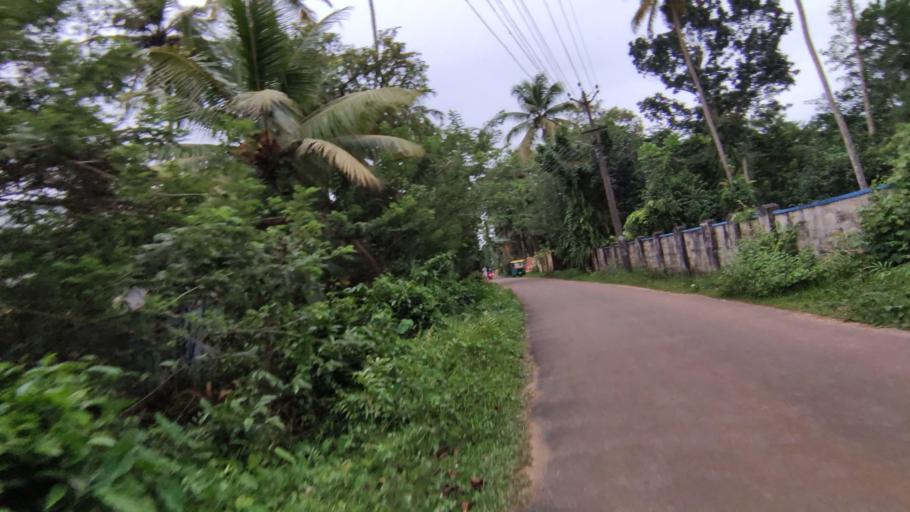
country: IN
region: Kerala
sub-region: Alappuzha
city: Shertallai
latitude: 9.6675
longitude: 76.3669
